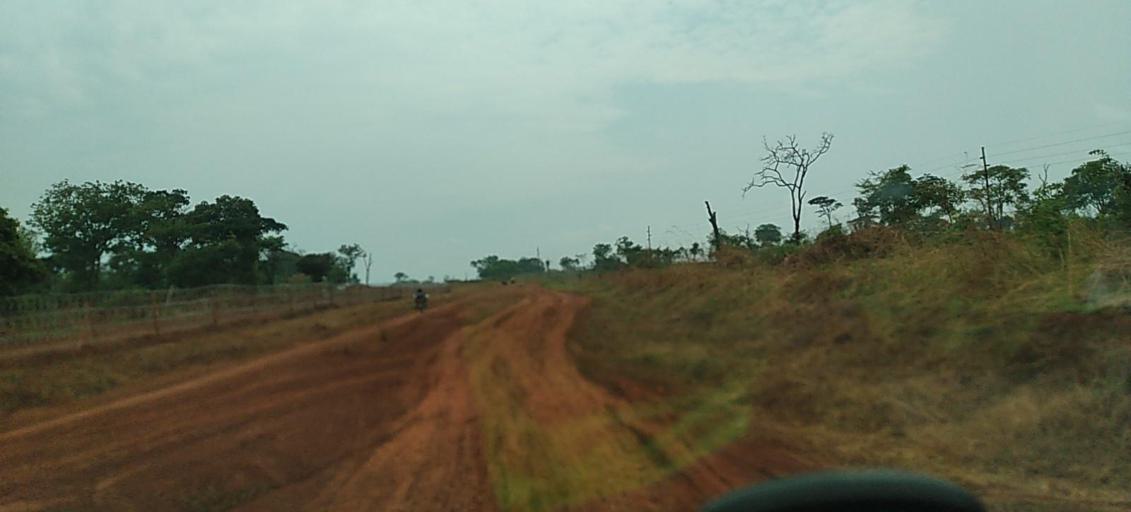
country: ZM
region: North-Western
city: Kansanshi
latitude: -12.0984
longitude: 26.4918
